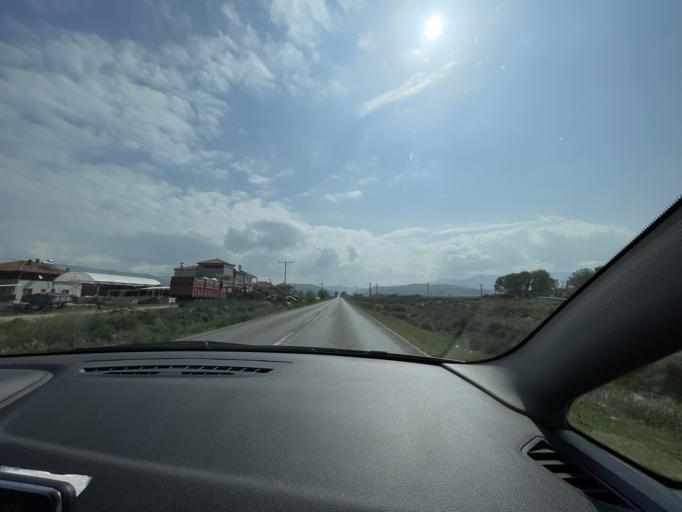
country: TR
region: Denizli
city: Acipayam
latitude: 37.5082
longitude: 29.4057
